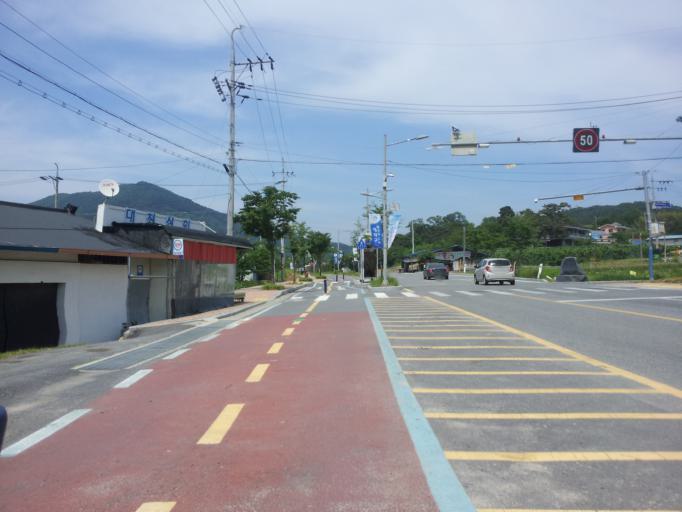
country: KR
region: Daejeon
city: Sintansin
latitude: 36.4667
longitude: 127.4689
